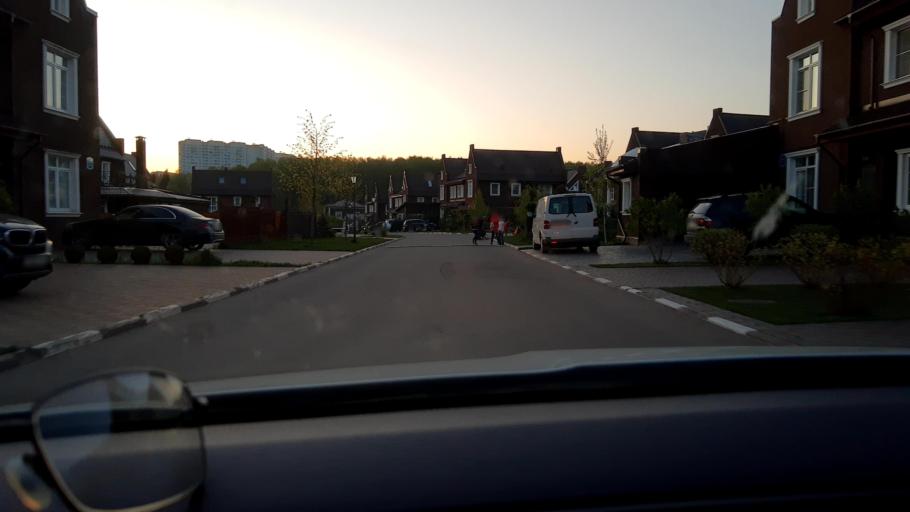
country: RU
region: Moskovskaya
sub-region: Leninskiy Rayon
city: Vnukovo
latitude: 55.6190
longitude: 37.3225
